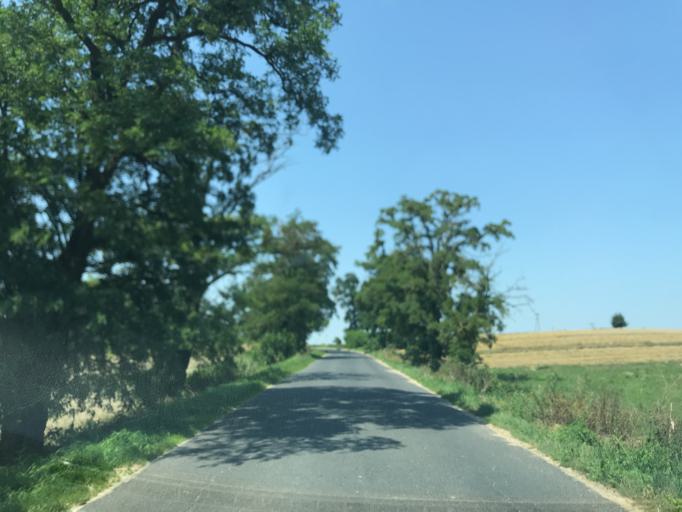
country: PL
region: Kujawsko-Pomorskie
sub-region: Powiat lipnowski
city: Chrostkowo
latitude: 52.9952
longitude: 19.2344
